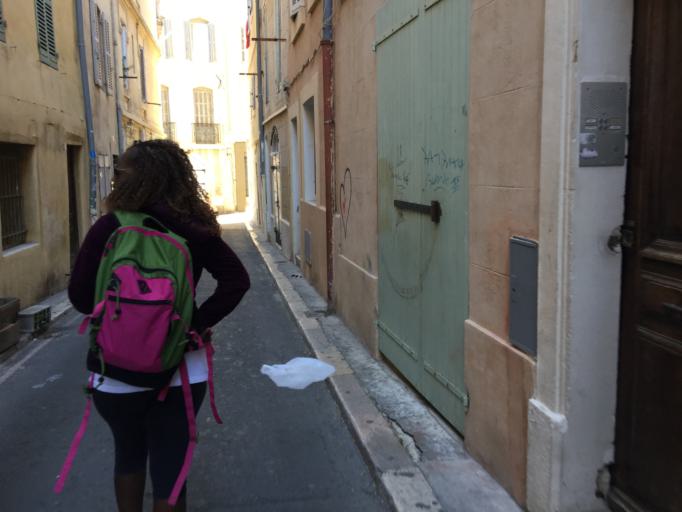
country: FR
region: Provence-Alpes-Cote d'Azur
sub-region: Departement des Bouches-du-Rhone
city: Marseille 02
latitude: 43.2991
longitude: 5.3679
